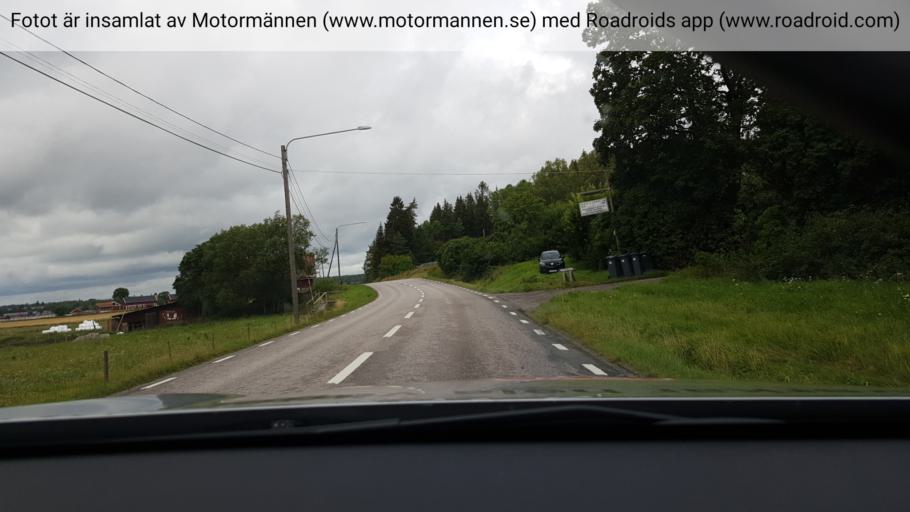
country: SE
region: Stockholm
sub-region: Norrtalje Kommun
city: Rimbo
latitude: 59.7386
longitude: 18.4012
